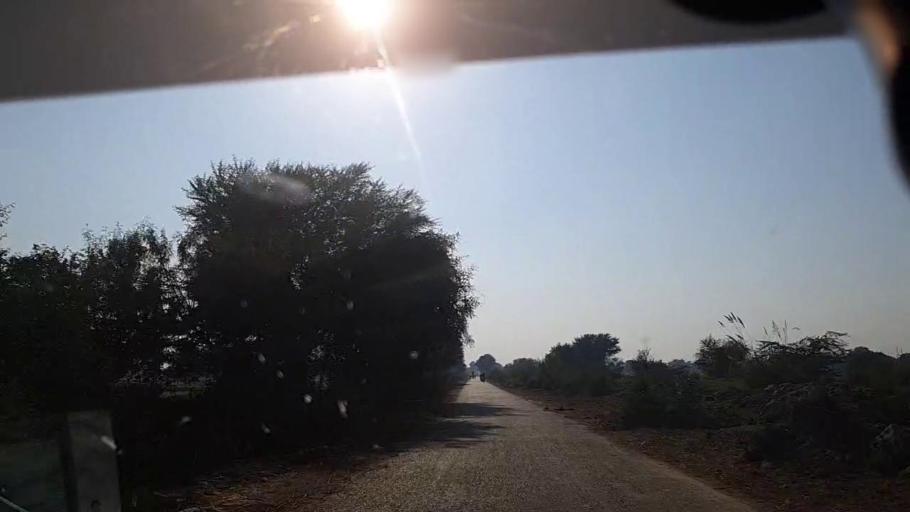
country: PK
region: Sindh
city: Sobhadero
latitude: 27.2417
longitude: 68.2855
